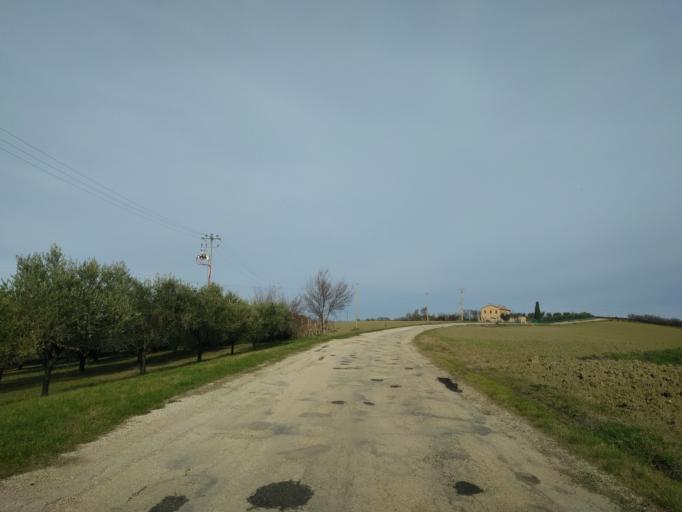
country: IT
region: The Marches
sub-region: Provincia di Pesaro e Urbino
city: Cuccurano
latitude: 43.8047
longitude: 12.9417
